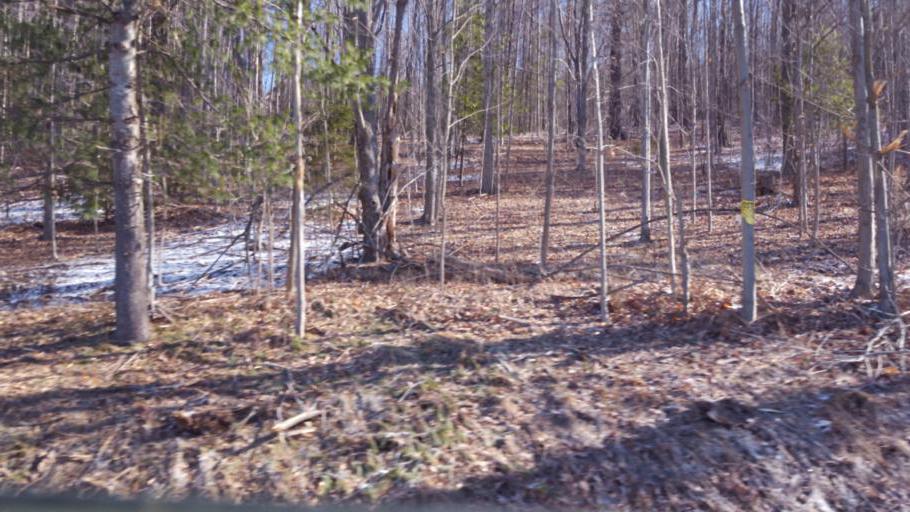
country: US
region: New York
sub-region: Allegany County
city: Wellsville
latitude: 42.1292
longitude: -77.9492
